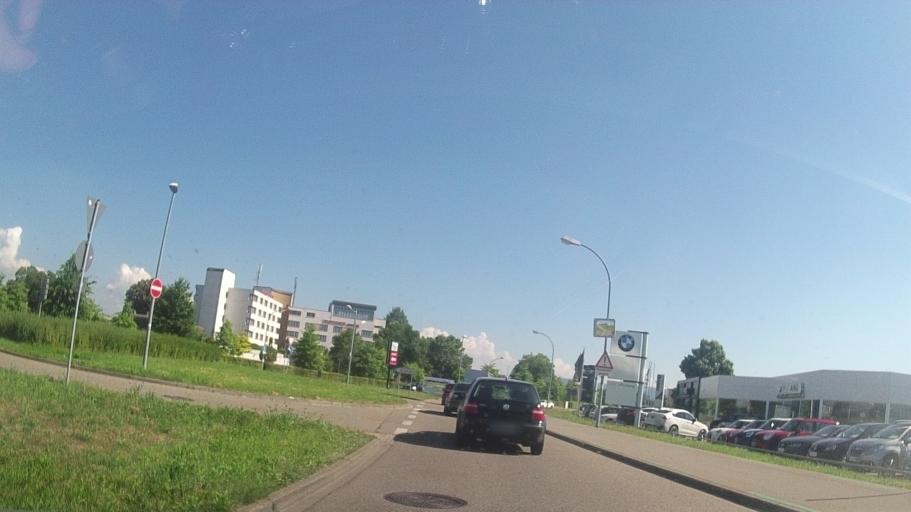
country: DE
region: Baden-Wuerttemberg
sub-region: Freiburg Region
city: Offenburg
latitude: 48.4659
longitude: 7.9319
